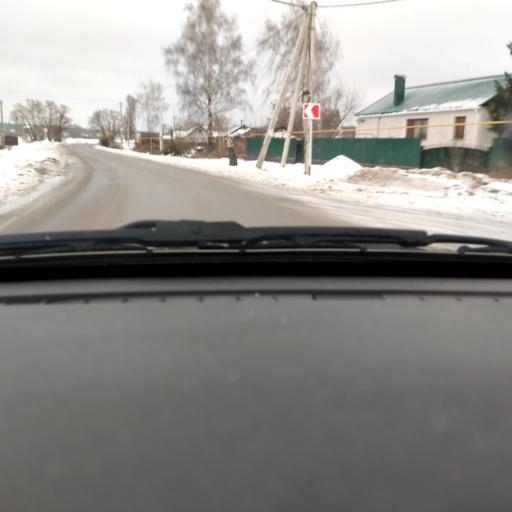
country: RU
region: Voronezj
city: Ramon'
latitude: 51.9080
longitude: 39.2845
